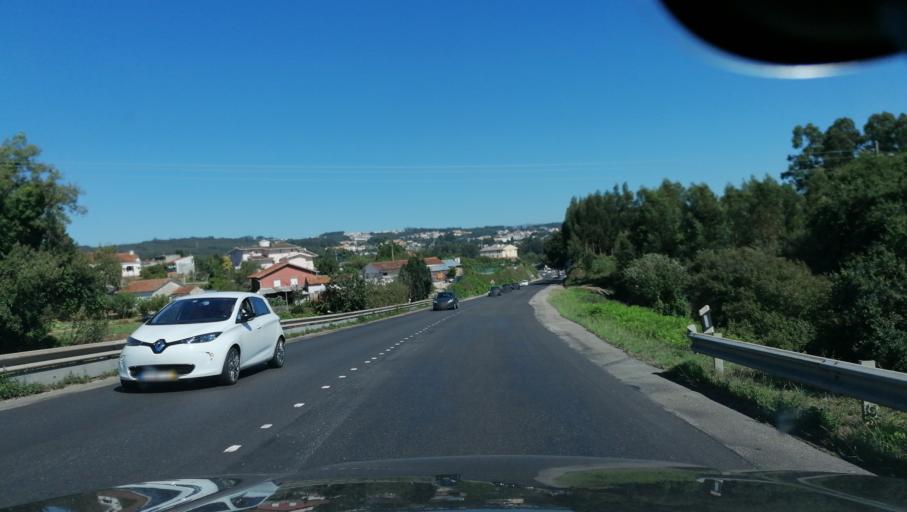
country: PT
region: Aveiro
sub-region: Santa Maria da Feira
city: Feira
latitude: 40.9331
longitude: -8.5422
